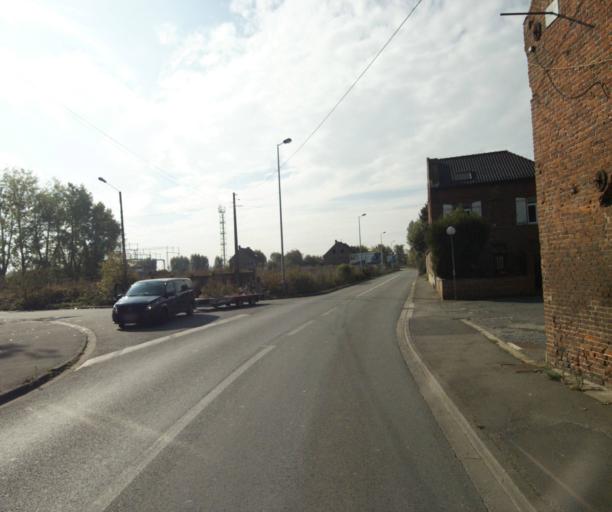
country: FR
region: Nord-Pas-de-Calais
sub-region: Departement du Nord
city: Seclin
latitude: 50.5447
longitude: 3.0447
